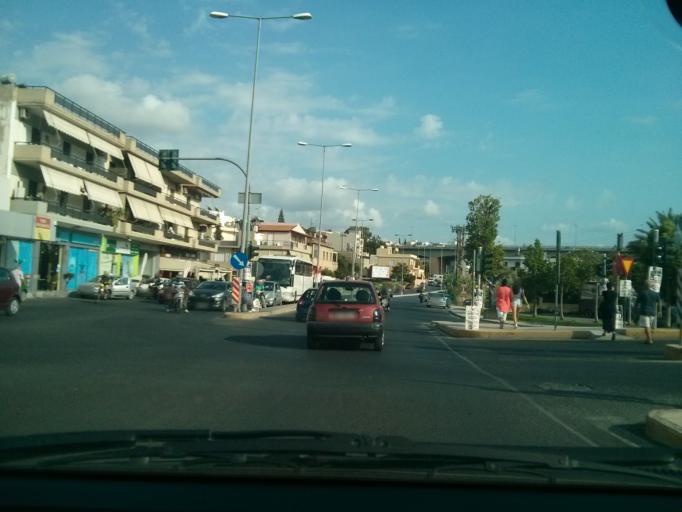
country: GR
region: Crete
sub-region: Nomos Irakleiou
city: Irakleion
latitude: 35.3226
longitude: 25.1419
